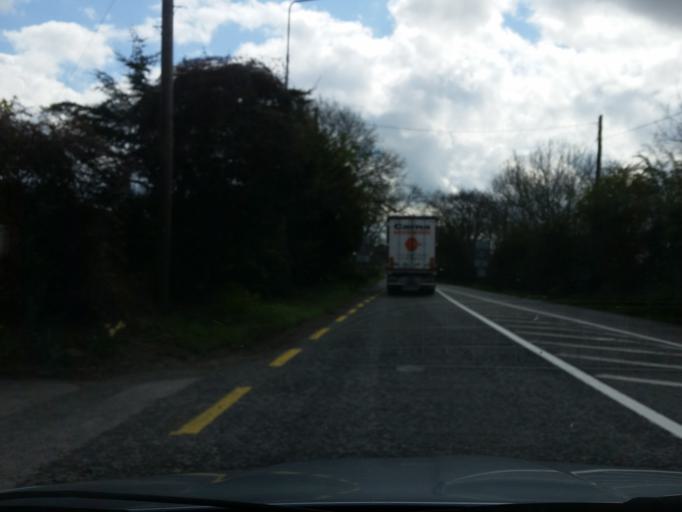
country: IE
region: Leinster
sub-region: An Mhi
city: Ratoath
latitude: 53.5576
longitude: -6.4395
